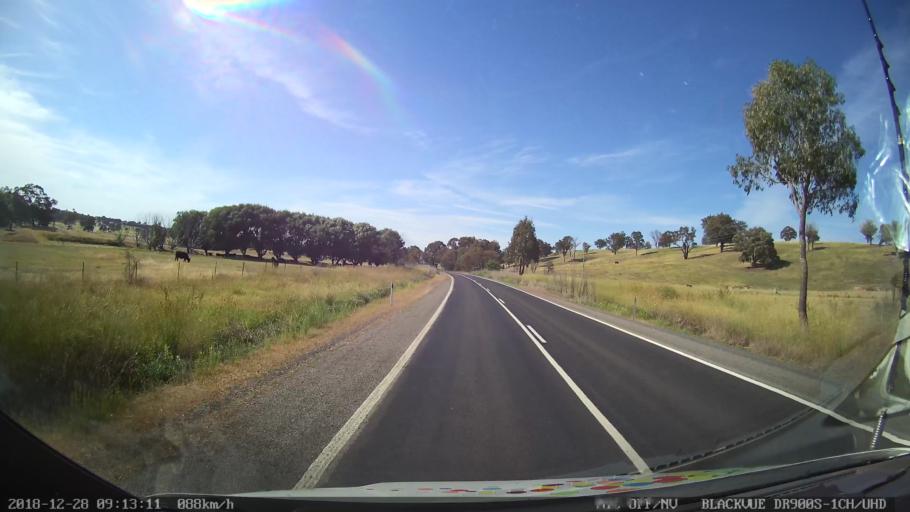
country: AU
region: New South Wales
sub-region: Upper Lachlan Shire
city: Crookwell
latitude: -34.2655
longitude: 149.3428
